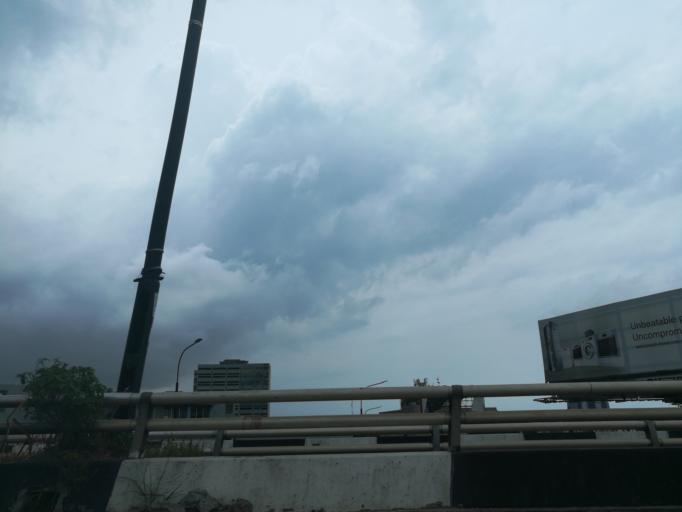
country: NG
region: Lagos
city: Lagos
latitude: 6.4449
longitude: 3.4067
